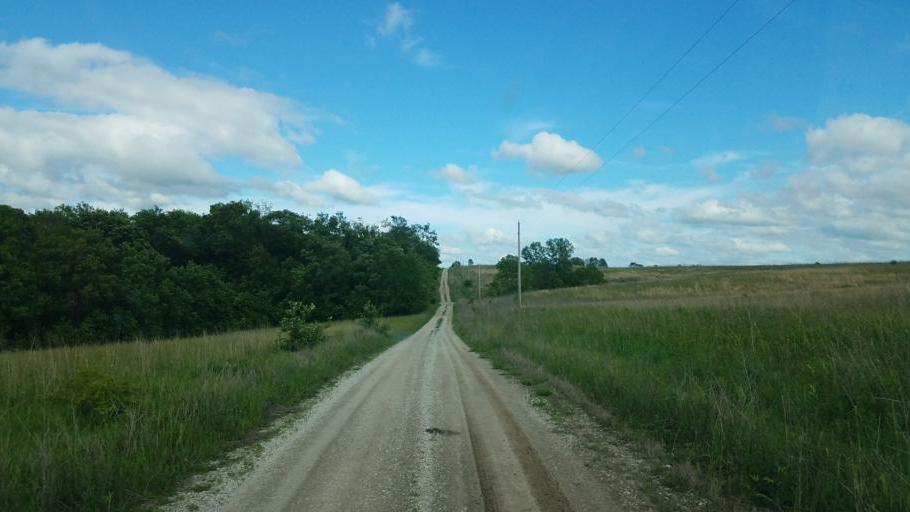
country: US
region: Missouri
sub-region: Mercer County
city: Princeton
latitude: 40.2602
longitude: -93.7068
